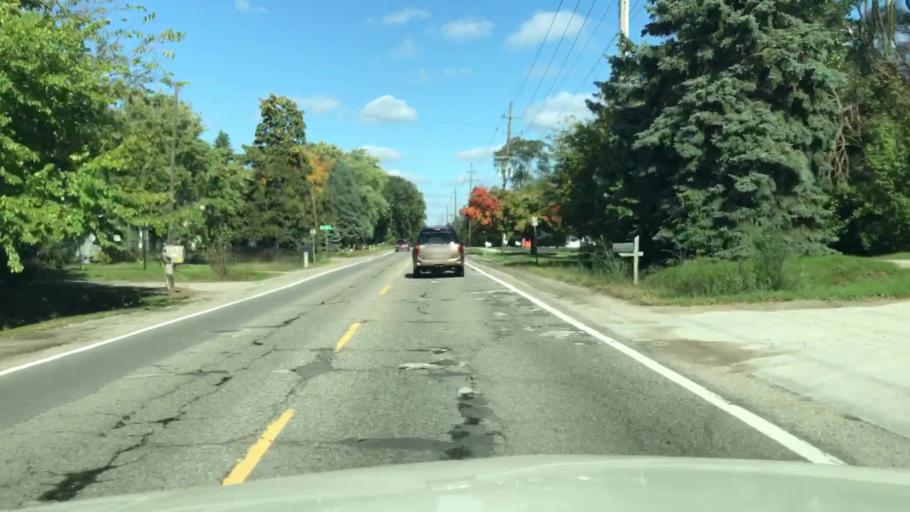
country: US
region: Michigan
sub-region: Oakland County
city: Rochester
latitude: 42.6411
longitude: -83.0922
